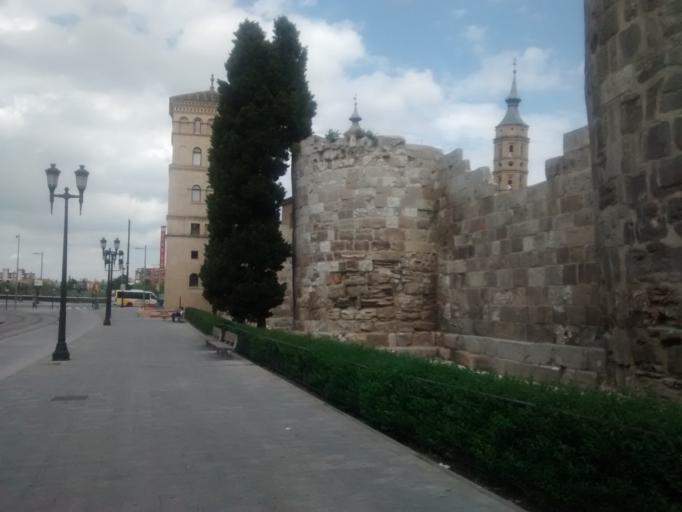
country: ES
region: Aragon
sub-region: Provincia de Zaragoza
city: Zaragoza
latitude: 41.6570
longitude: -0.8821
